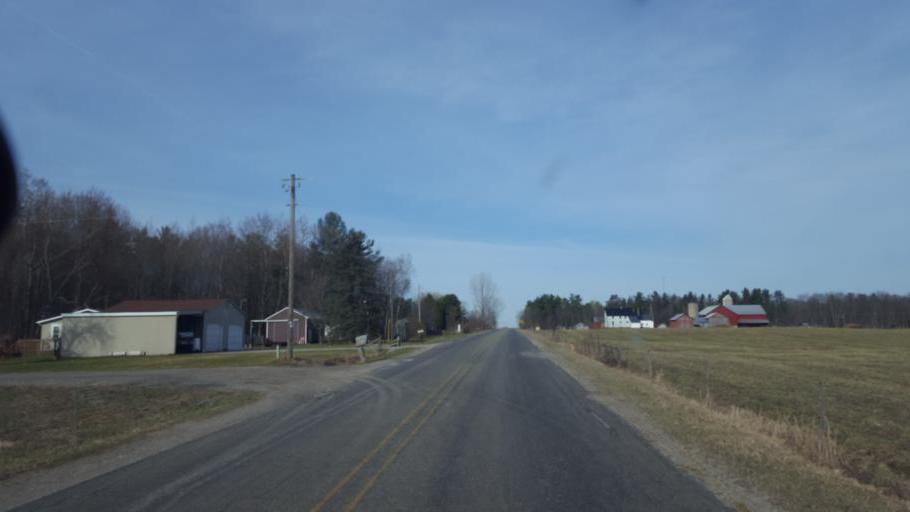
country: US
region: Michigan
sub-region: Montcalm County
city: Howard City
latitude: 43.5260
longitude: -85.4770
